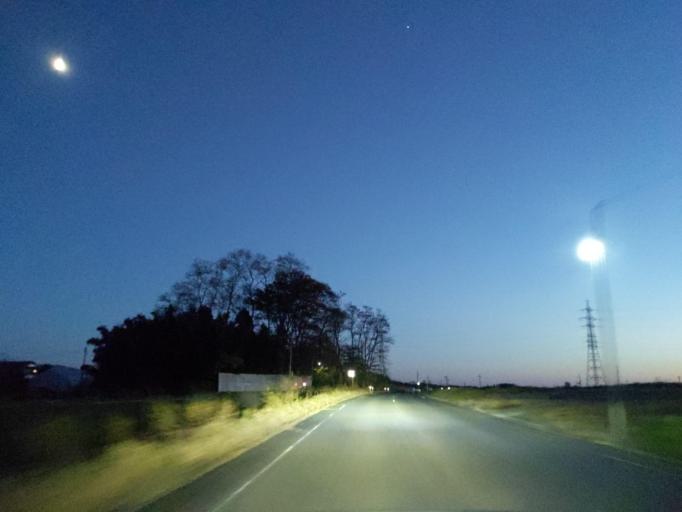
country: JP
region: Fukushima
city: Sukagawa
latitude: 37.3246
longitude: 140.3899
